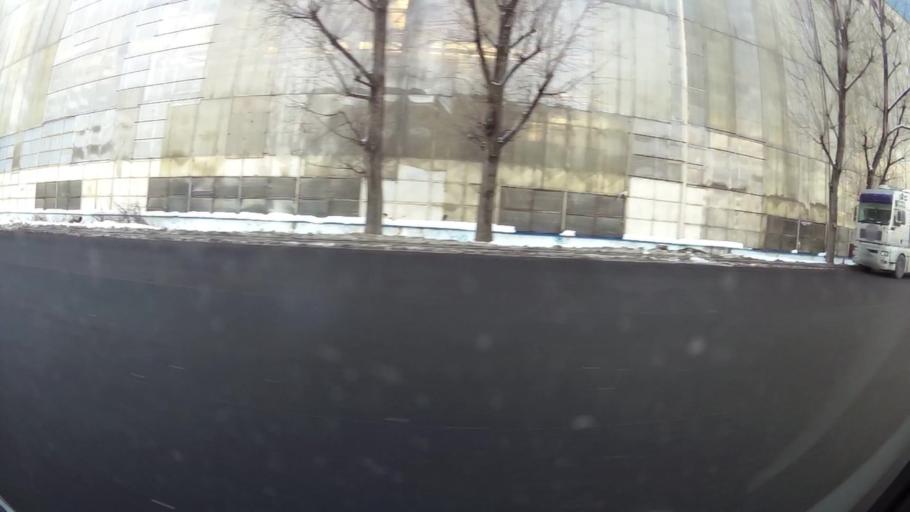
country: RO
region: Ilfov
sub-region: Comuna Popesti-Leordeni
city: Popesti-Leordeni
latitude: 44.3655
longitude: 26.1456
